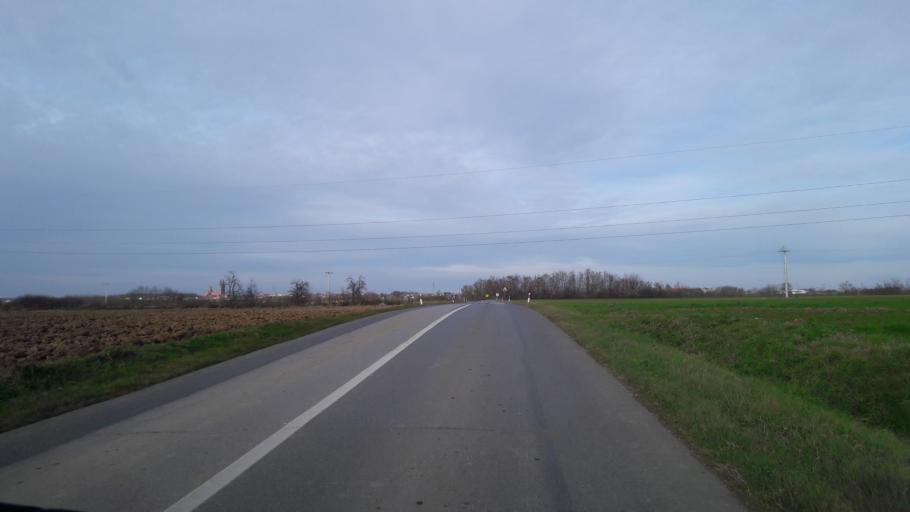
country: HR
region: Osjecko-Baranjska
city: Piskorevci
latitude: 45.2879
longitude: 18.4331
